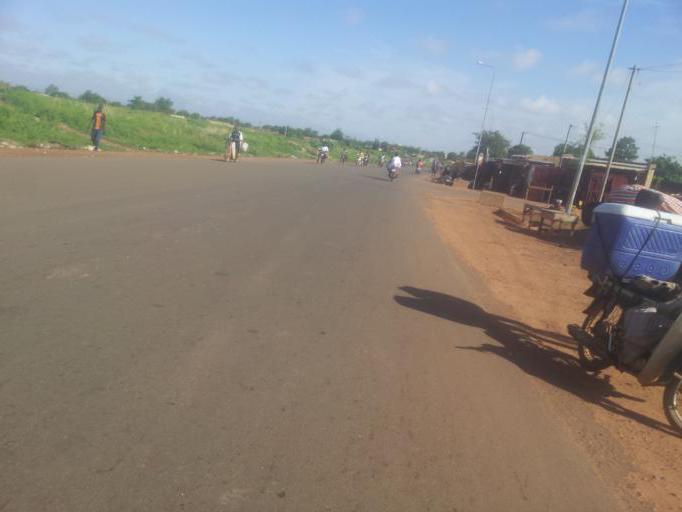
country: BF
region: Centre
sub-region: Kadiogo Province
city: Ouagadougou
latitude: 12.3711
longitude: -1.5675
